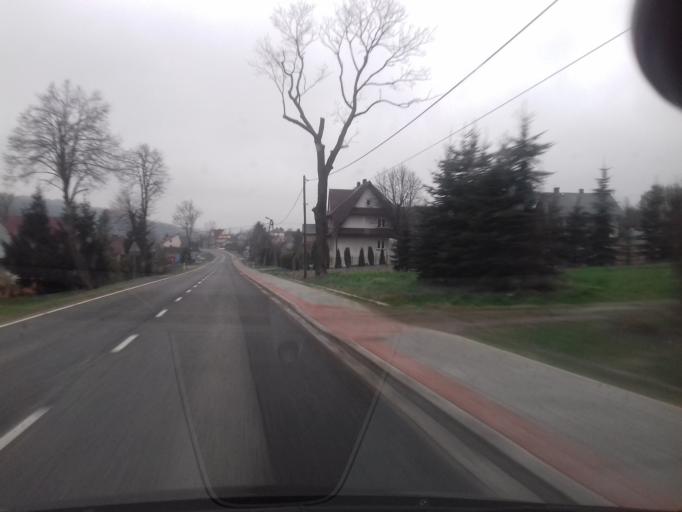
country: PL
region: Lesser Poland Voivodeship
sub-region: Powiat limanowski
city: Mszana Gorna
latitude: 49.6928
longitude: 20.1186
